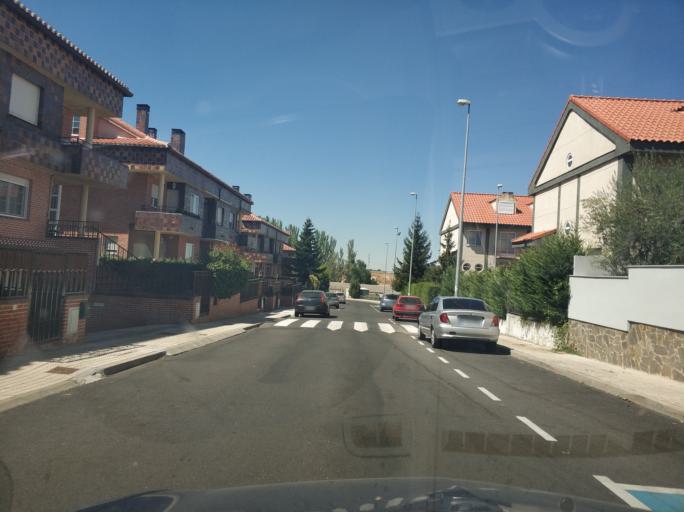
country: ES
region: Castille and Leon
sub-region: Provincia de Salamanca
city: Villares de la Reina
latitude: 40.9950
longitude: -5.6556
